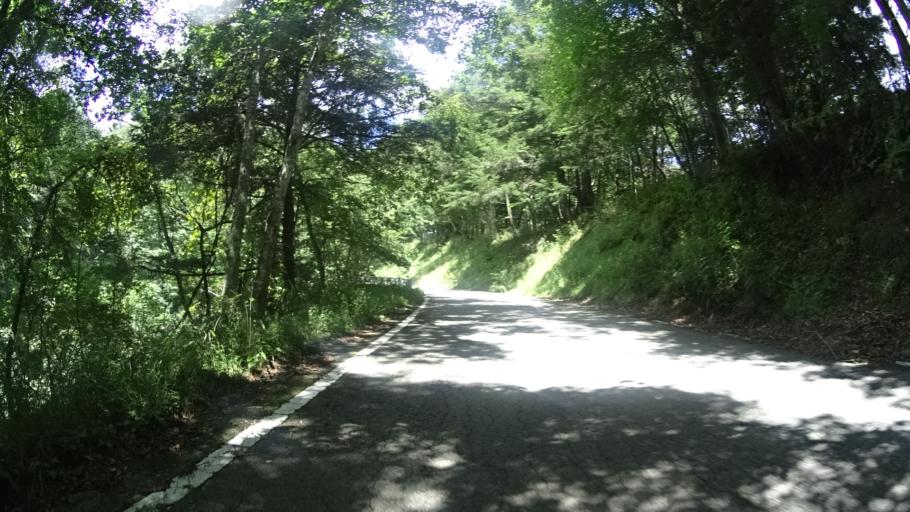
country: JP
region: Yamanashi
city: Enzan
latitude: 35.8196
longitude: 138.6513
